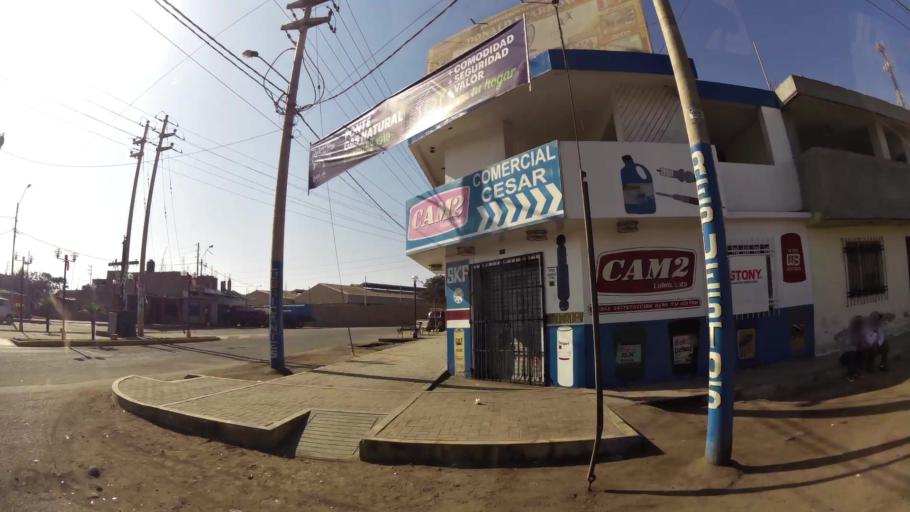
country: PE
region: Ica
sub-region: Provincia de Chincha
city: Chincha Alta
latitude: -13.3981
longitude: -76.1279
